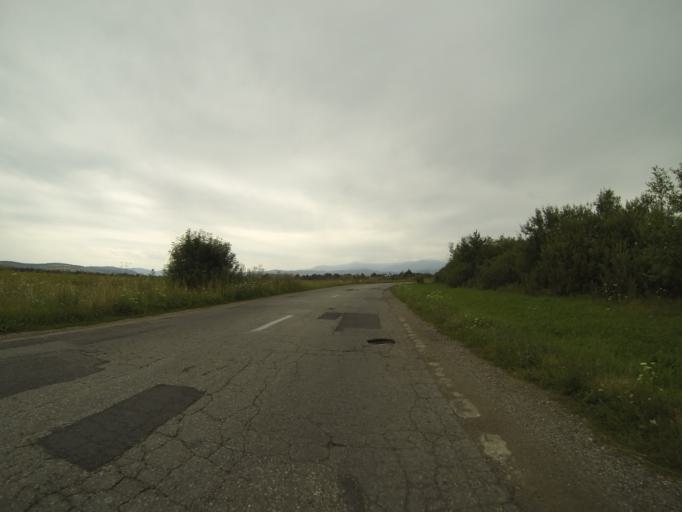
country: RO
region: Brasov
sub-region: Comuna Sinca Veche
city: Sinca Veche
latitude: 45.7774
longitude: 25.1490
